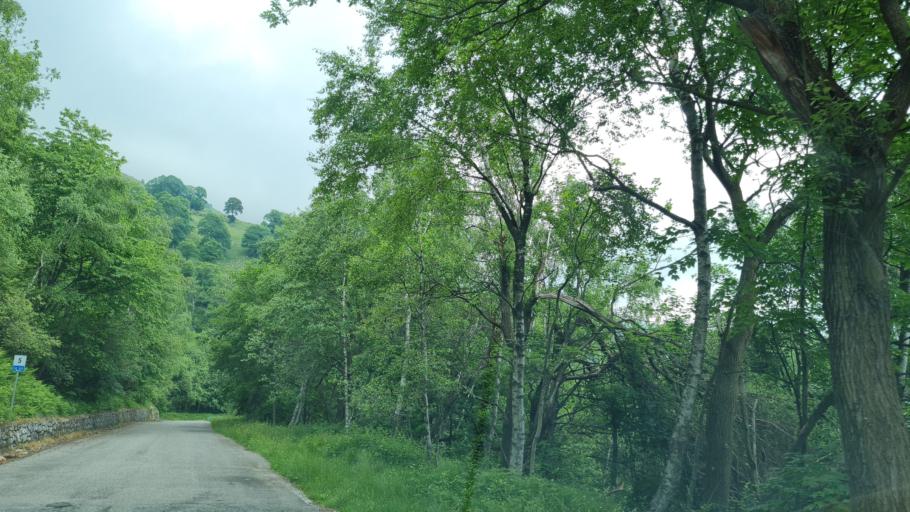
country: IT
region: Piedmont
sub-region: Provincia di Biella
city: Sordevolo
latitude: 45.5961
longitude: 7.9751
